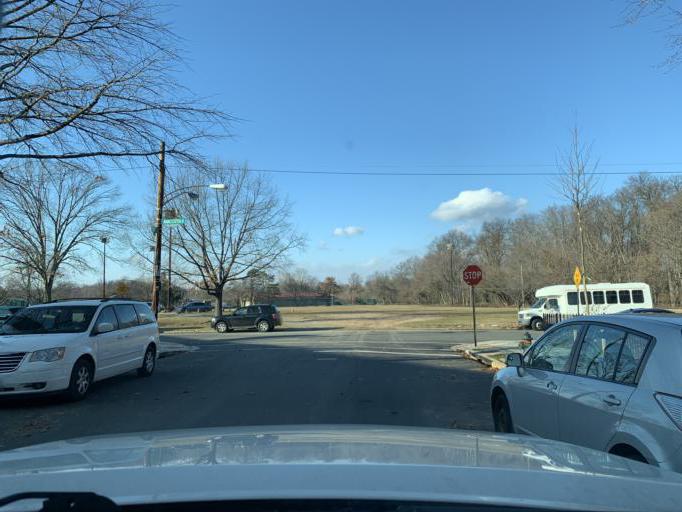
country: US
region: Maryland
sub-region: Prince George's County
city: Colmar Manor
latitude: 38.9129
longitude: -76.9380
